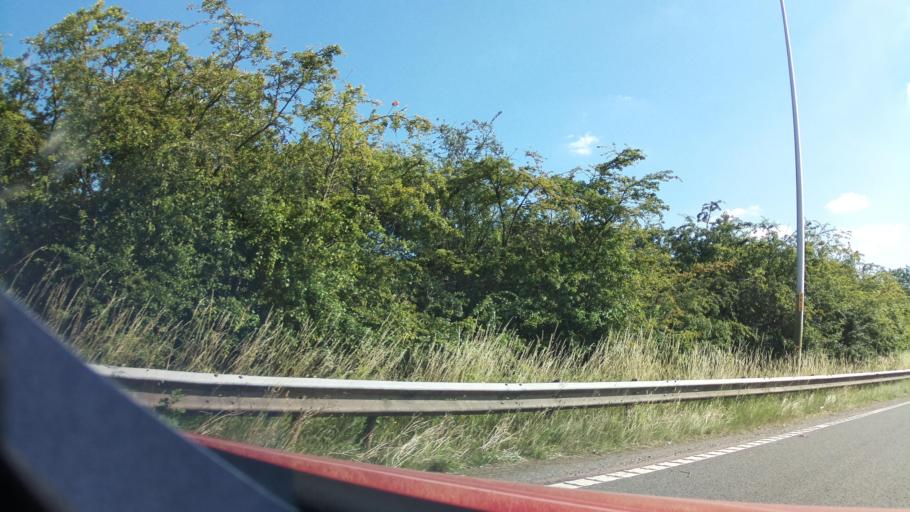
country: GB
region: England
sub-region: Worcestershire
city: Droitwich
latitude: 52.2874
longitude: -2.1175
